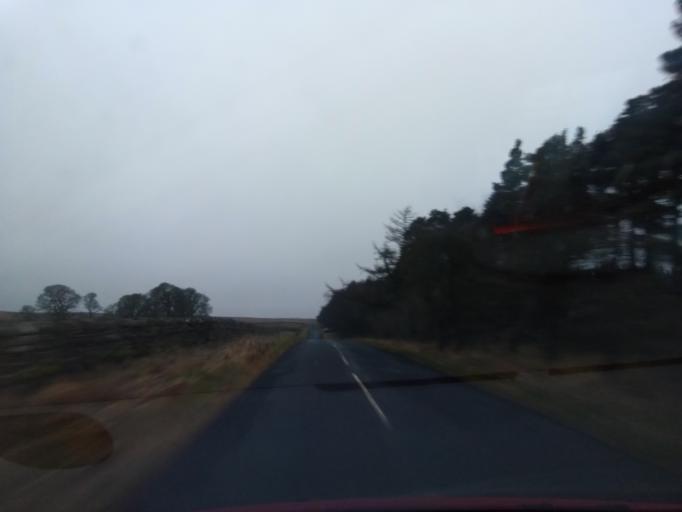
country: GB
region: England
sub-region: Northumberland
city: Otterburn
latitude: 55.2088
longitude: -2.0422
